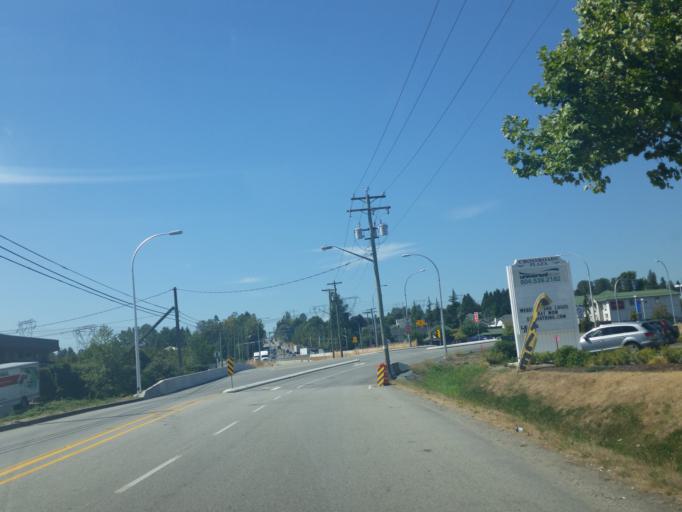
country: CA
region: British Columbia
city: Langley
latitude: 49.1045
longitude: -122.6875
